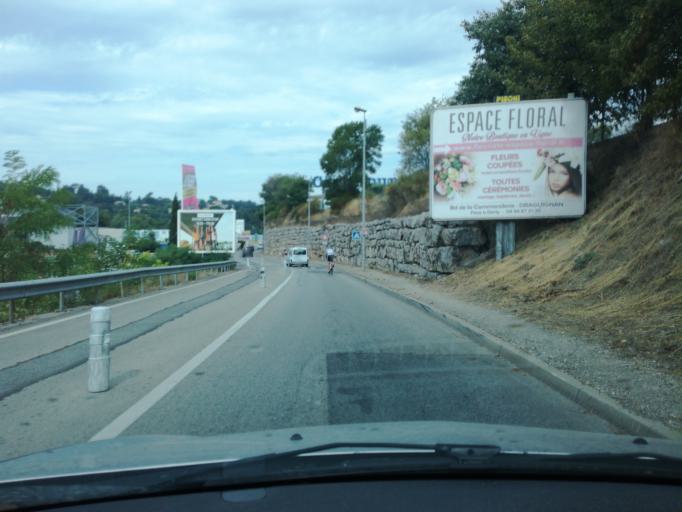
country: FR
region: Provence-Alpes-Cote d'Azur
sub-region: Departement du Var
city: Draguignan
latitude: 43.5273
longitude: 6.4530
